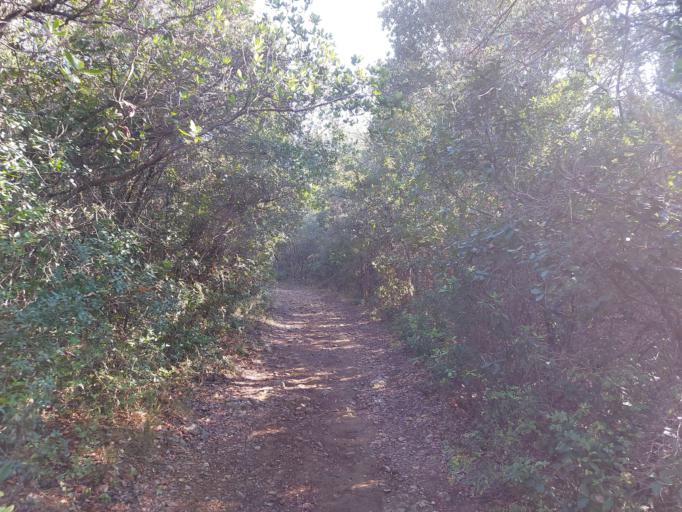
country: HR
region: Dubrovacko-Neretvanska
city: Smokvica
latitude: 42.7618
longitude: 16.8081
